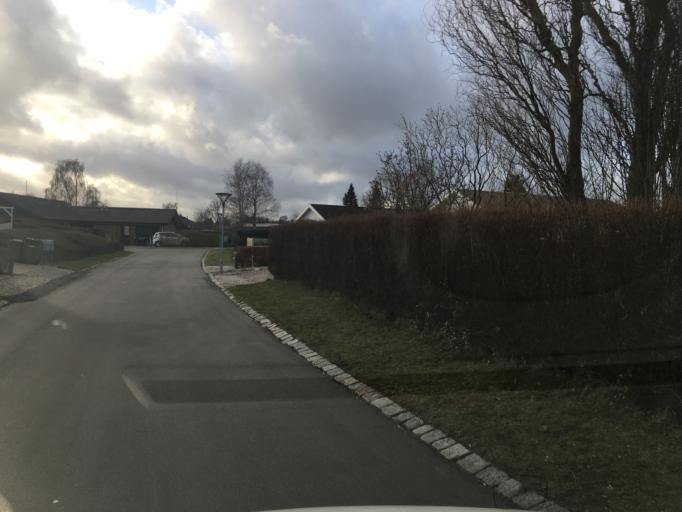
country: DK
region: South Denmark
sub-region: Sonderborg Kommune
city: Grasten
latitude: 54.9799
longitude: 9.5131
